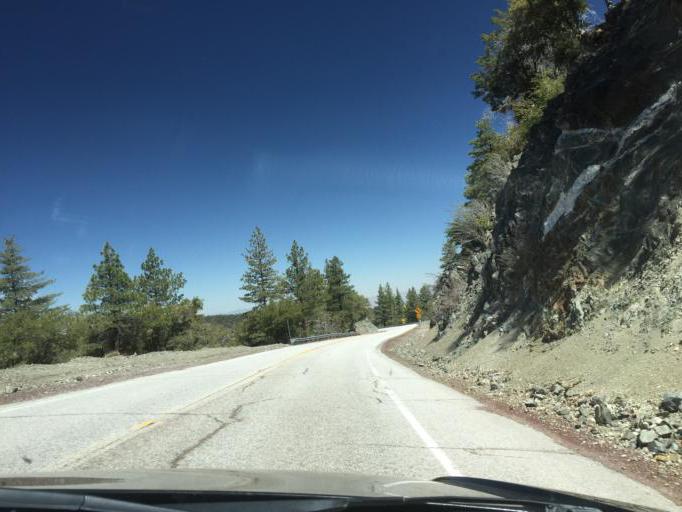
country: US
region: California
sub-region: San Bernardino County
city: Pinon Hills
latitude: 34.3894
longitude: -117.7092
